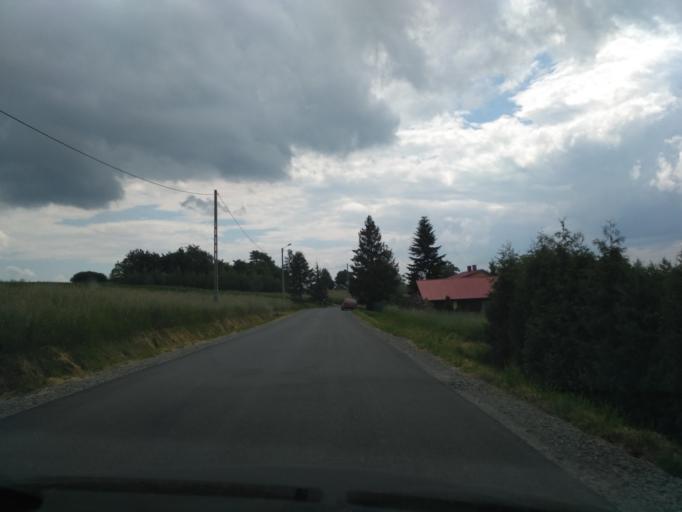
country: PL
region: Subcarpathian Voivodeship
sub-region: Powiat rzeszowski
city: Hyzne
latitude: 49.9378
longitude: 22.1773
